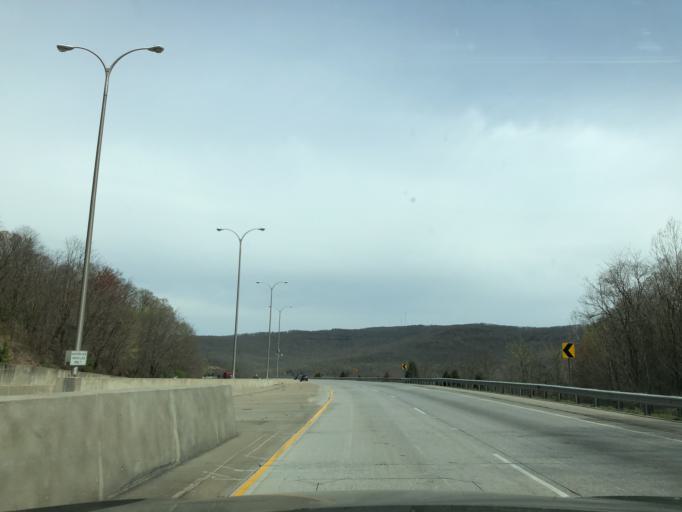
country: US
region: Arkansas
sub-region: Washington County
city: West Fork
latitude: 35.7658
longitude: -94.1905
